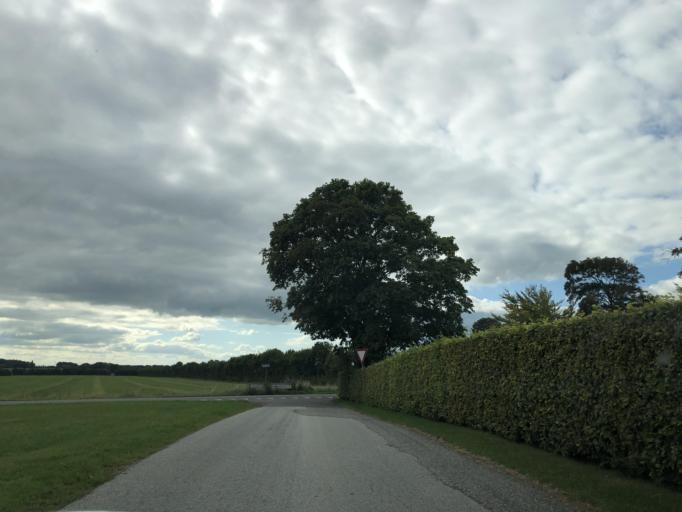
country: DK
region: North Denmark
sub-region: Alborg Kommune
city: Nibe
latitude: 56.8426
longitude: 9.6910
